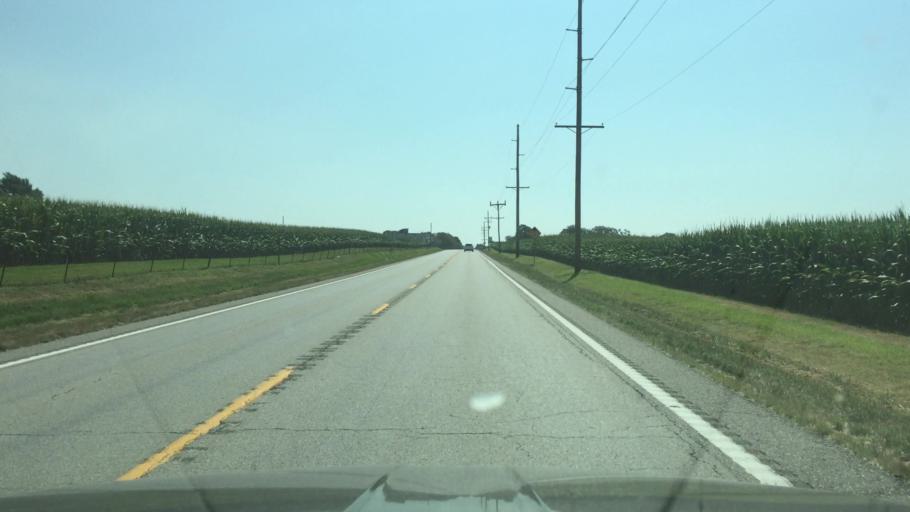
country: US
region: Missouri
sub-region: Moniteau County
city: Tipton
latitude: 38.6698
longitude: -92.8884
